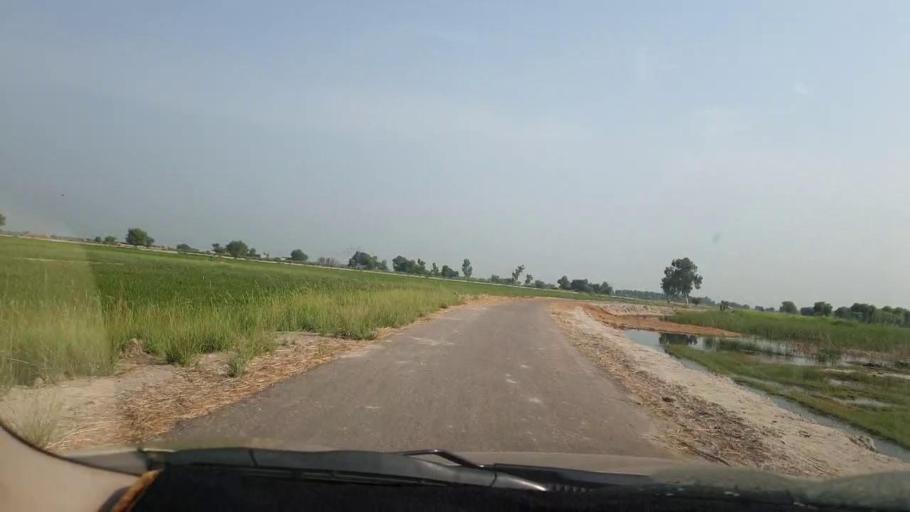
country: PK
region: Sindh
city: Goth Garelo
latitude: 27.4690
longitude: 68.0781
